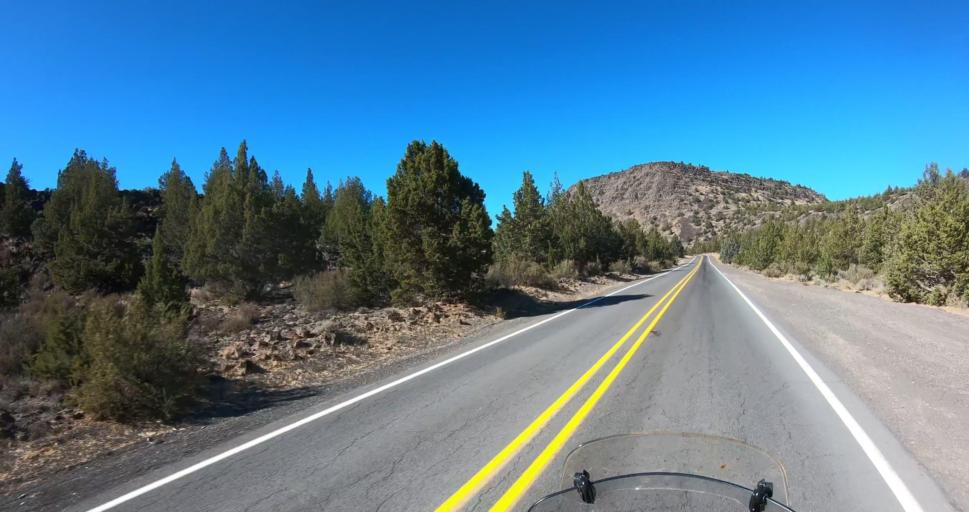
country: US
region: Oregon
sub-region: Deschutes County
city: La Pine
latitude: 43.0416
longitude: -120.7956
